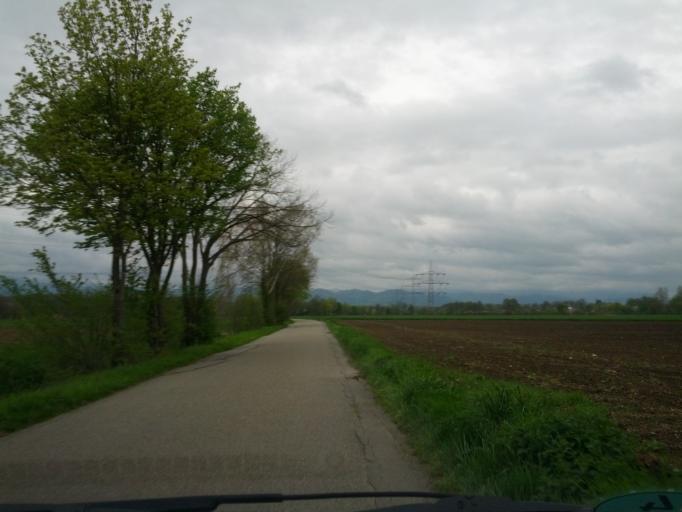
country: DE
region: Baden-Wuerttemberg
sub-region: Freiburg Region
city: Merdingen
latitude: 47.9900
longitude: 7.7217
